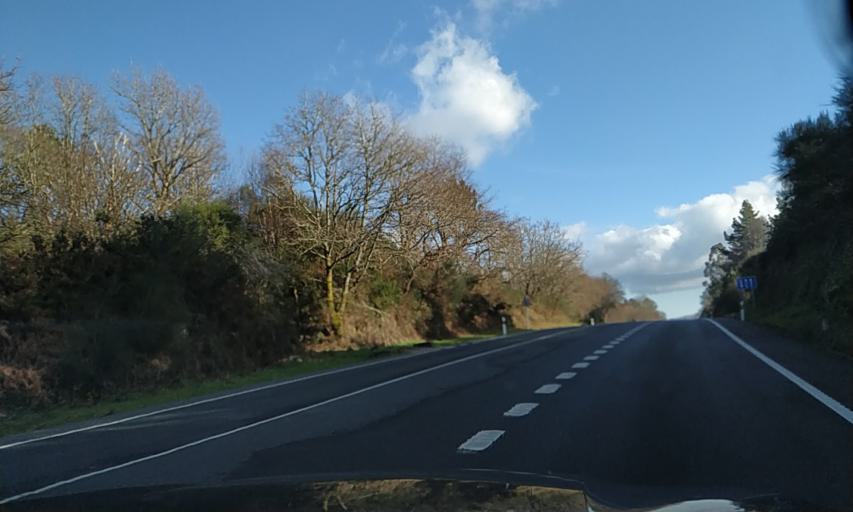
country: ES
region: Galicia
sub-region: Provincia de Pontevedra
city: Silleda
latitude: 42.7080
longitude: -8.3471
